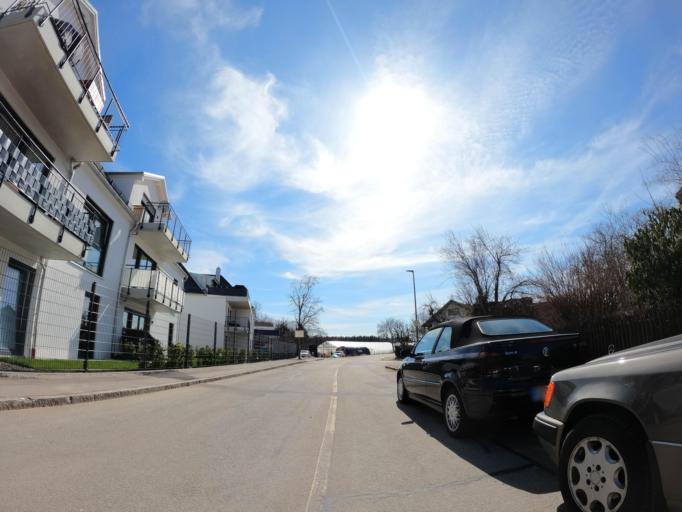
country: DE
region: Bavaria
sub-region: Upper Bavaria
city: Hohenkirchen-Siegertsbrunn
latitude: 48.0142
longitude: 11.7135
